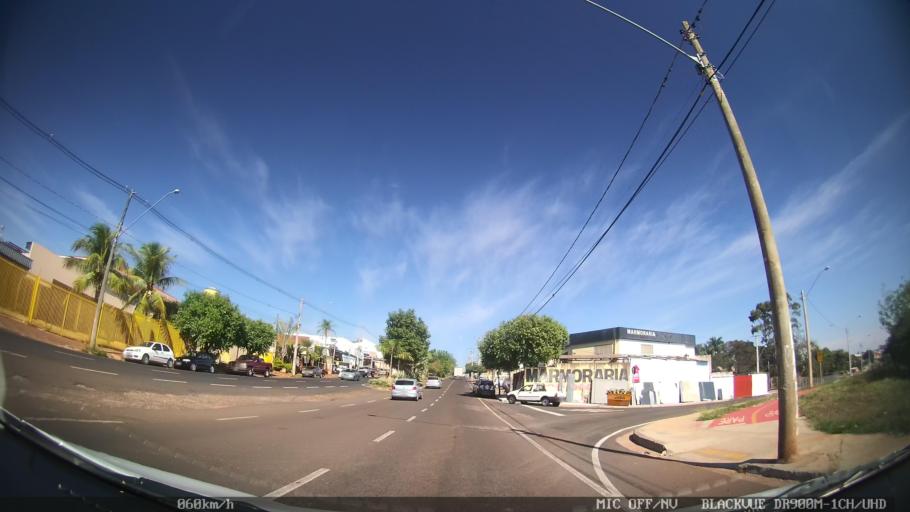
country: BR
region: Sao Paulo
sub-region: Sao Jose Do Rio Preto
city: Sao Jose do Rio Preto
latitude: -20.7701
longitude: -49.3600
